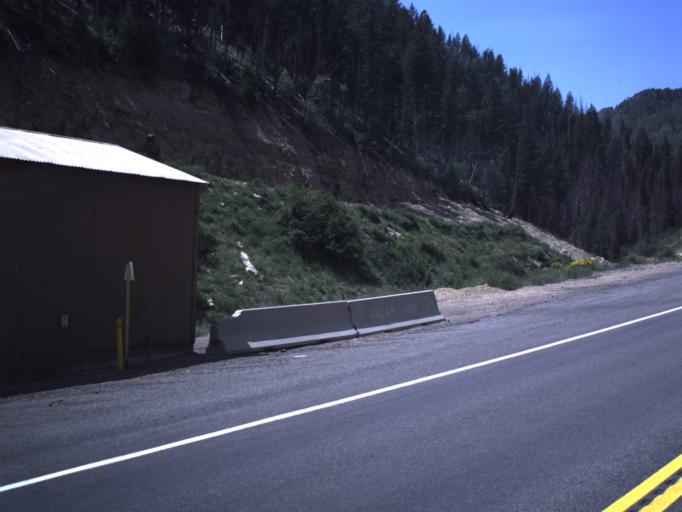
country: US
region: Utah
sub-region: Sanpete County
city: Fairview
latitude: 39.6823
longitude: -111.1848
